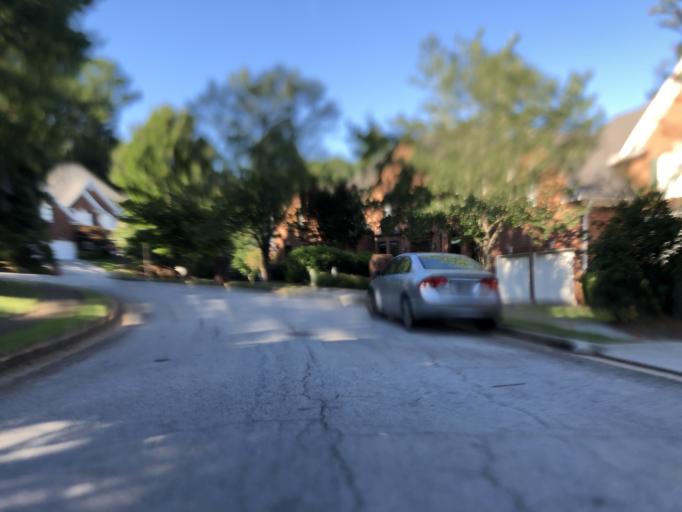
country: US
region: Georgia
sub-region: DeKalb County
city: North Decatur
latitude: 33.7875
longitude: -84.3141
